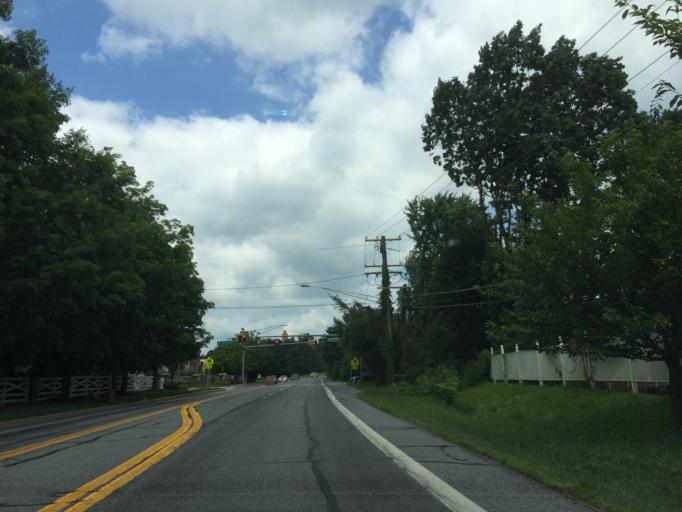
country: US
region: Maryland
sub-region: Howard County
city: Columbia
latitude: 39.3034
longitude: -76.8664
